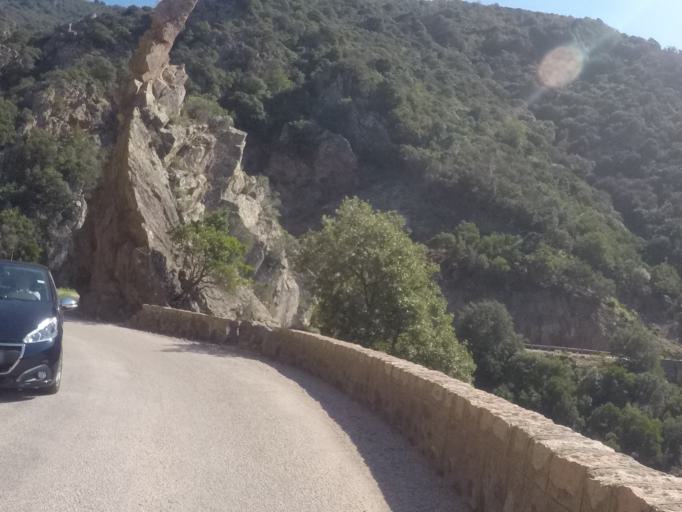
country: FR
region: Corsica
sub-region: Departement de la Corse-du-Sud
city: Cargese
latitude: 42.3413
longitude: 8.6599
